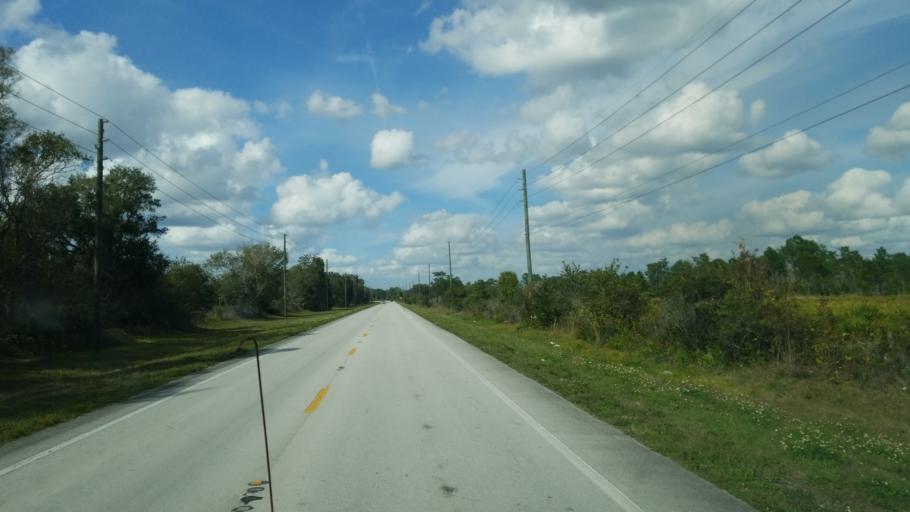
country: US
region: Florida
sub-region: Osceola County
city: Saint Cloud
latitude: 28.0849
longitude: -81.0718
